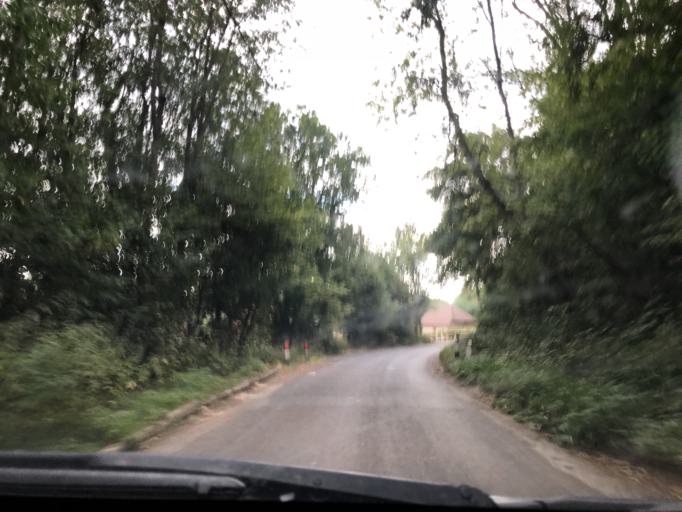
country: GB
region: England
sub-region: Kent
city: Sevenoaks
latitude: 51.2359
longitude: 0.2196
